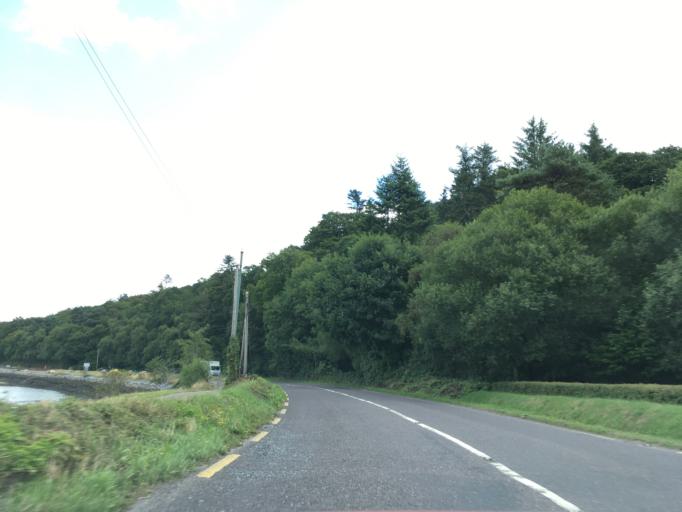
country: IE
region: Munster
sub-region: County Cork
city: Crosshaven
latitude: 51.8012
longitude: -8.3275
